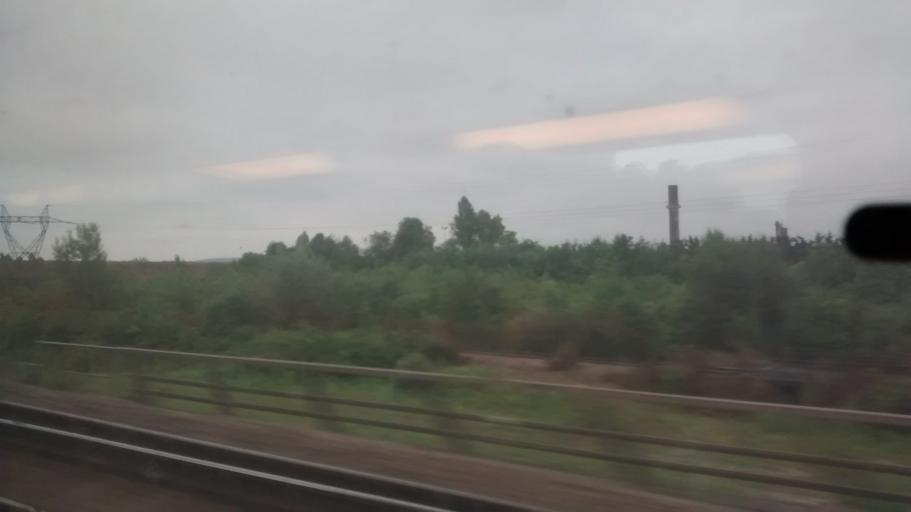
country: FR
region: Ile-de-France
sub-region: Departement de Seine-et-Marne
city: Saint-Germain-Laval
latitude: 48.3905
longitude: 2.9862
